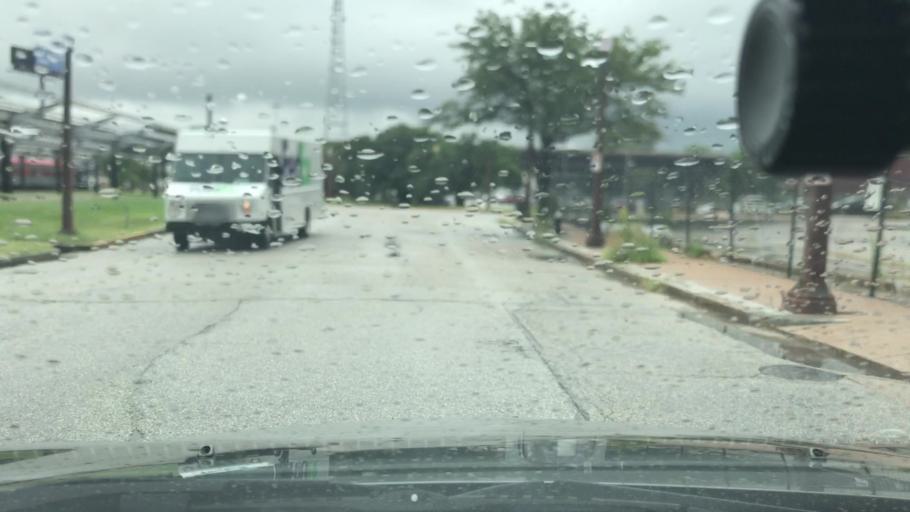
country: US
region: Missouri
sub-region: City of Saint Louis
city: St. Louis
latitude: 38.6278
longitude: -90.2099
